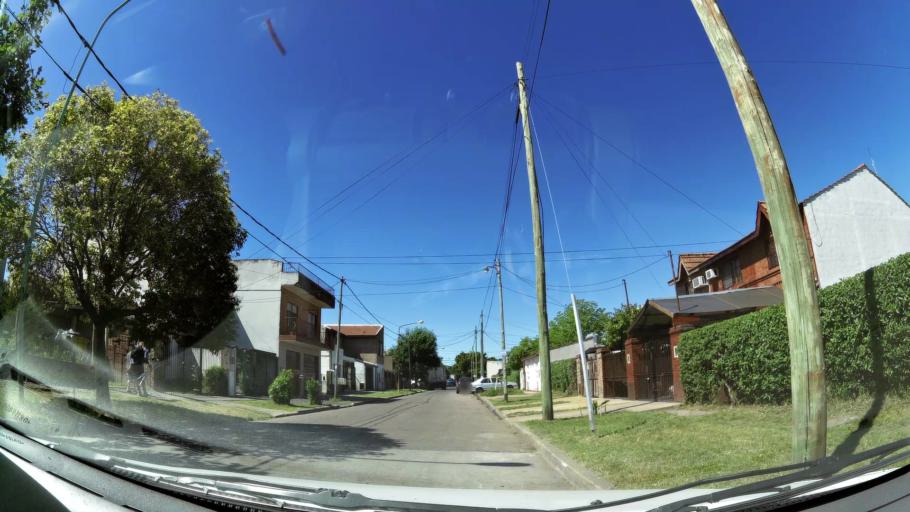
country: AR
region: Buenos Aires
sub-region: Partido de General San Martin
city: General San Martin
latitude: -34.5253
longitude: -58.5625
